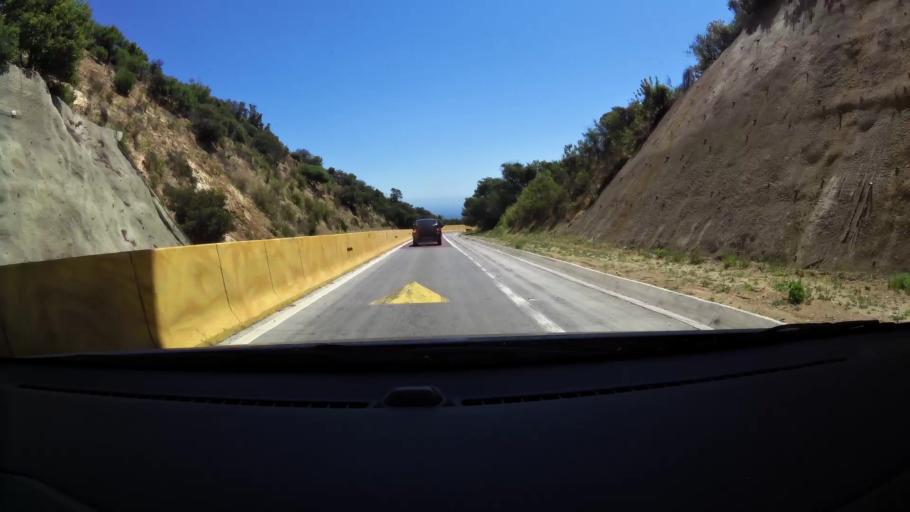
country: CL
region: Valparaiso
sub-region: Provincia de Valparaiso
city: Valparaiso
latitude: -33.0592
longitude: -71.6522
